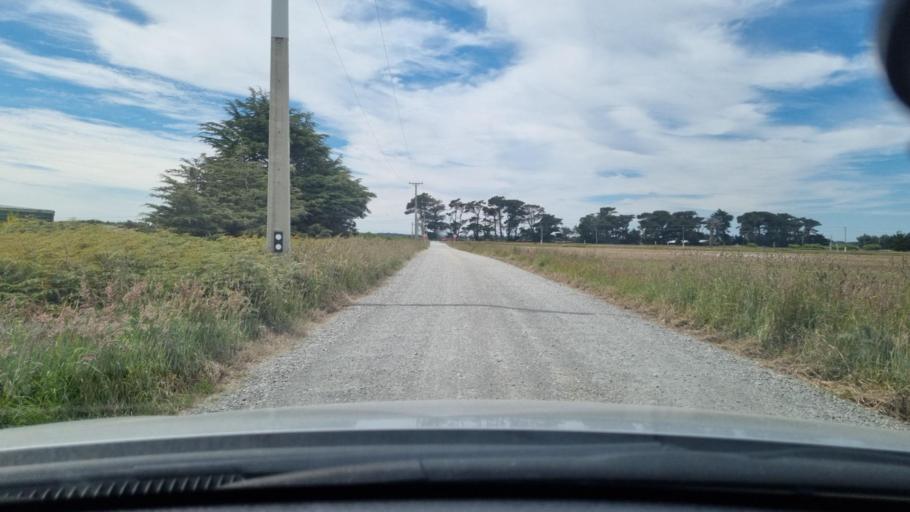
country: NZ
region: Southland
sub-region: Invercargill City
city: Invercargill
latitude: -46.4053
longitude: 168.2899
